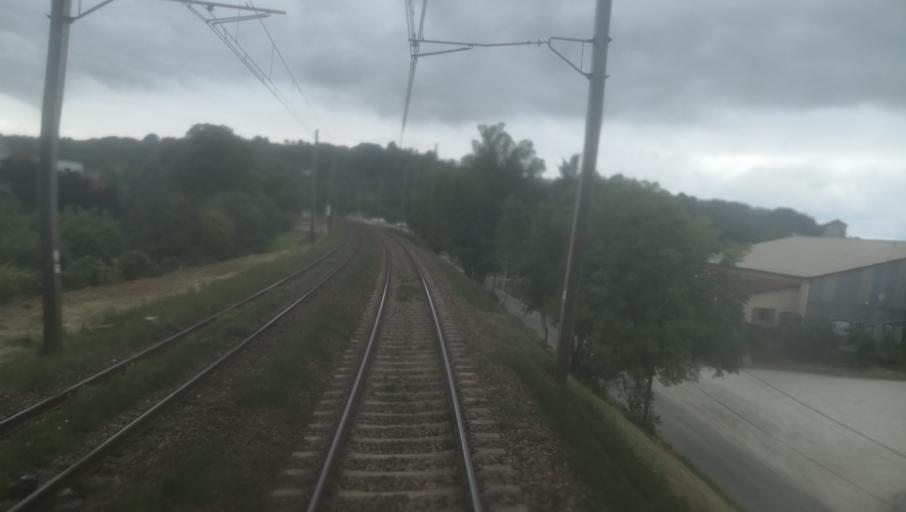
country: FR
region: Midi-Pyrenees
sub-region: Departement du Tarn-et-Garonne
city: Moissac
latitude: 44.1024
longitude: 1.1045
